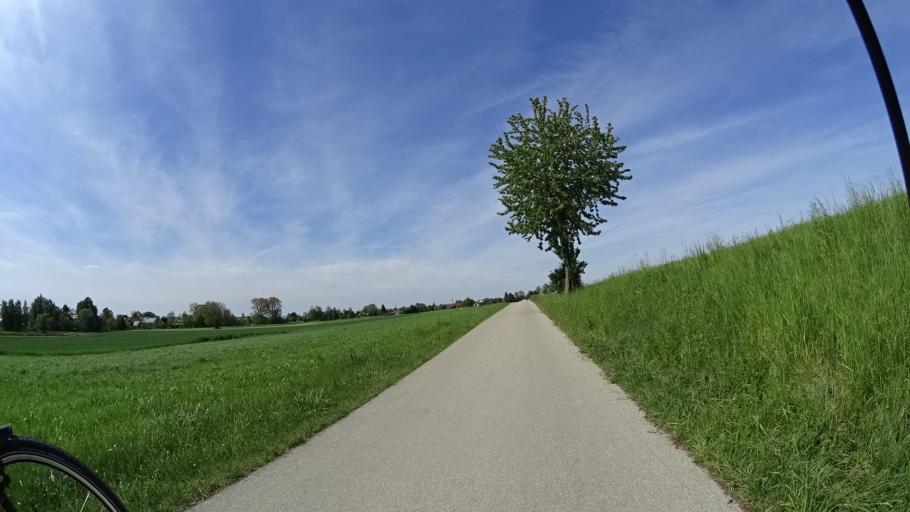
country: DE
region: Bavaria
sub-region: Swabia
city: Pfaffenhofen an der Roth
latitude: 48.3381
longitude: 10.1603
